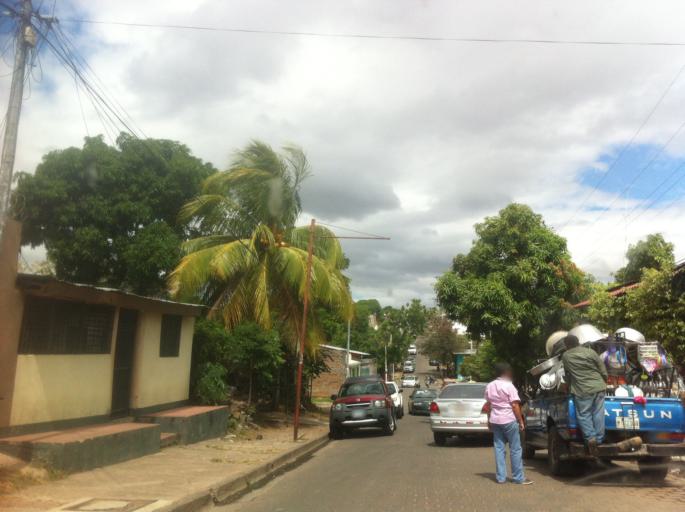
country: NI
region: Chontales
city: Juigalpa
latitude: 12.0993
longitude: -85.3620
